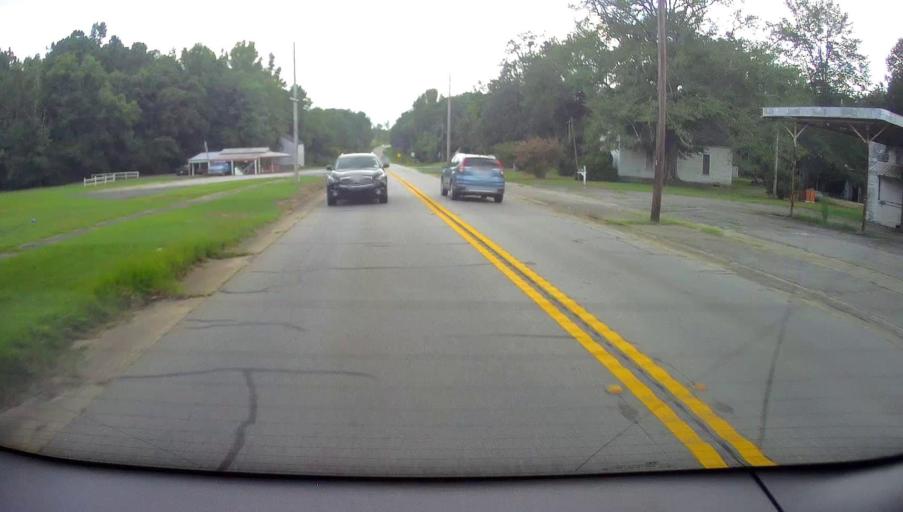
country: US
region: Georgia
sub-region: Coweta County
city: Senoia
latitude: 33.1684
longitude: -84.5807
